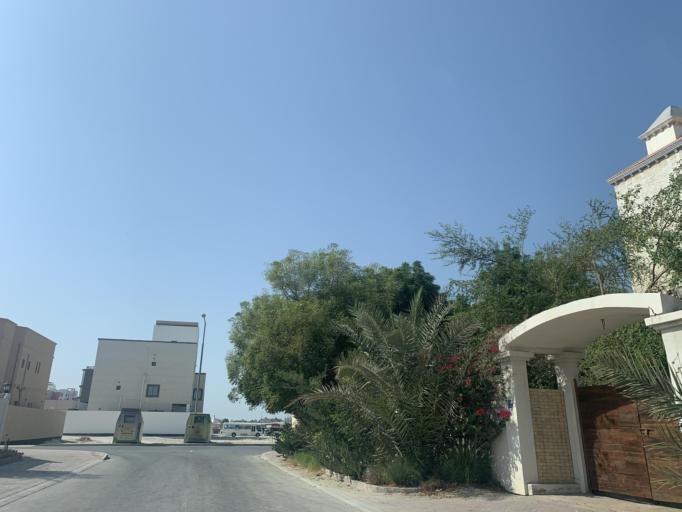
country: BH
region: Central Governorate
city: Madinat Hamad
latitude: 26.1389
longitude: 50.4927
